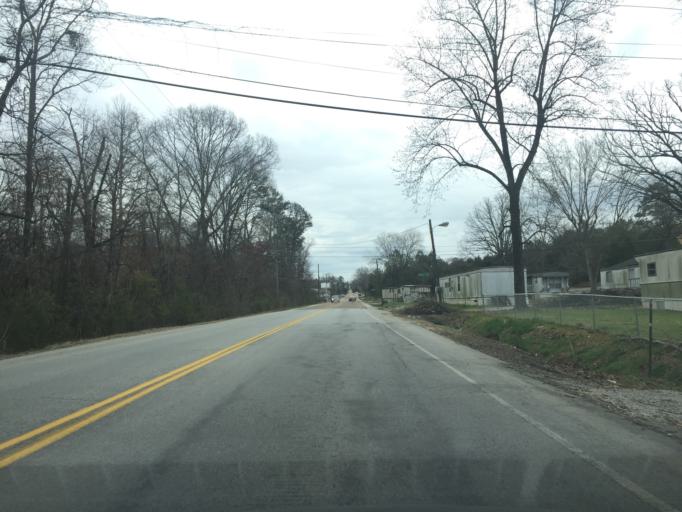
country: US
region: Tennessee
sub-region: Hamilton County
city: Harrison
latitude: 35.0700
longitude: -85.1160
